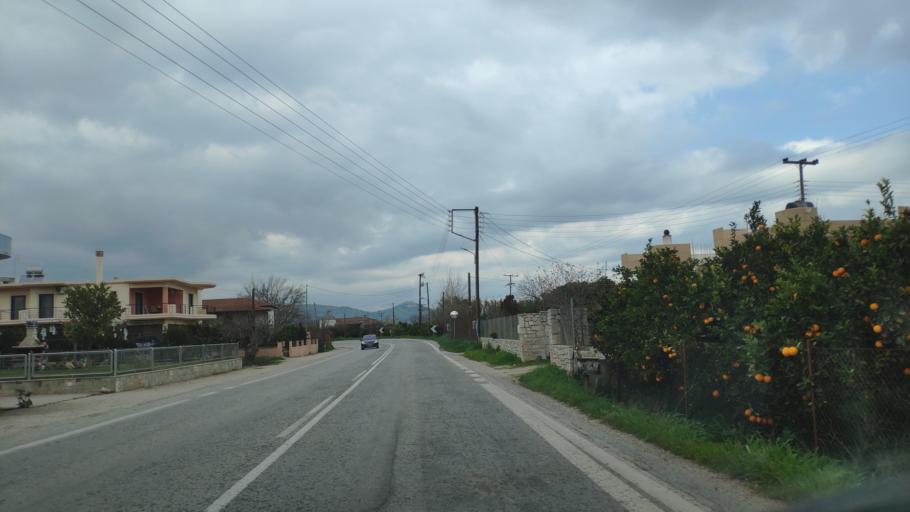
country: GR
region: Peloponnese
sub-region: Nomos Argolidos
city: Nea Kios
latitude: 37.5839
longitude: 22.7098
